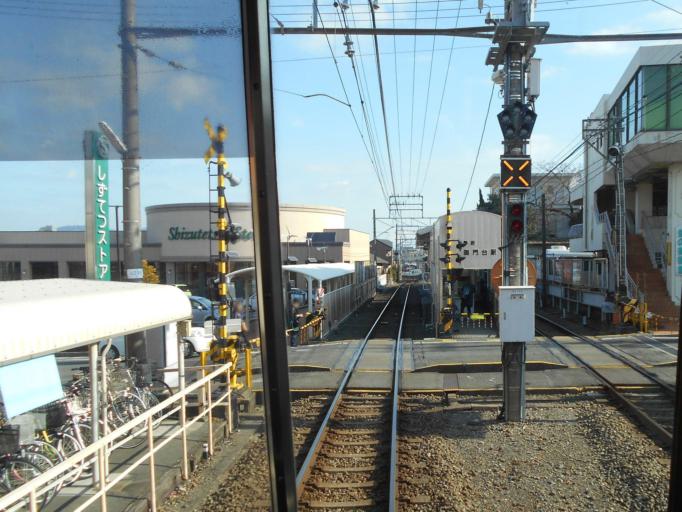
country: JP
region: Shizuoka
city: Shizuoka-shi
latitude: 35.0076
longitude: 138.4520
